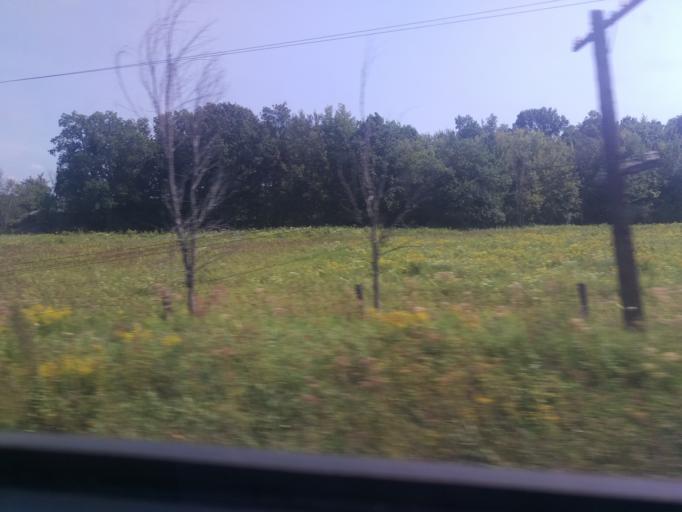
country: US
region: New York
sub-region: Jefferson County
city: Alexandria Bay
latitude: 44.4512
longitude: -75.9342
